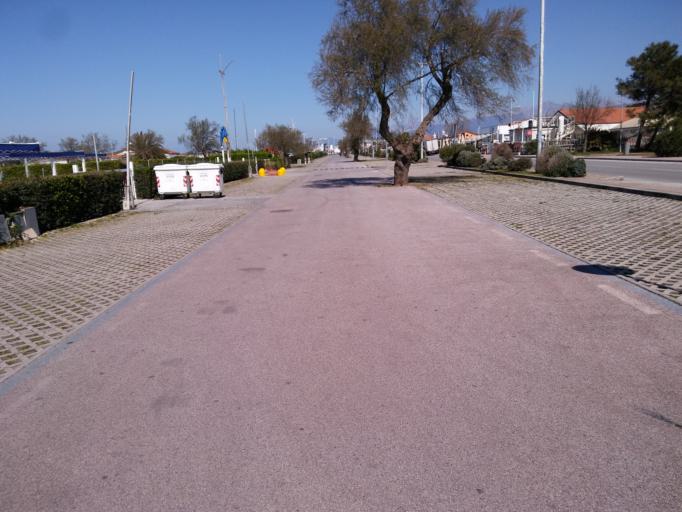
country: IT
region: Tuscany
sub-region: Provincia di Lucca
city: Viareggio
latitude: 43.8490
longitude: 10.2464
